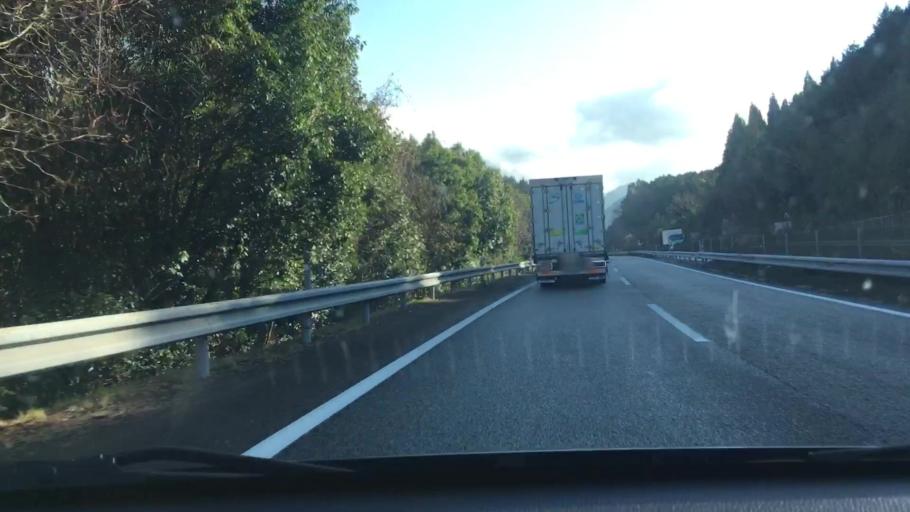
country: JP
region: Kumamoto
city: Hitoyoshi
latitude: 32.1678
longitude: 130.7929
